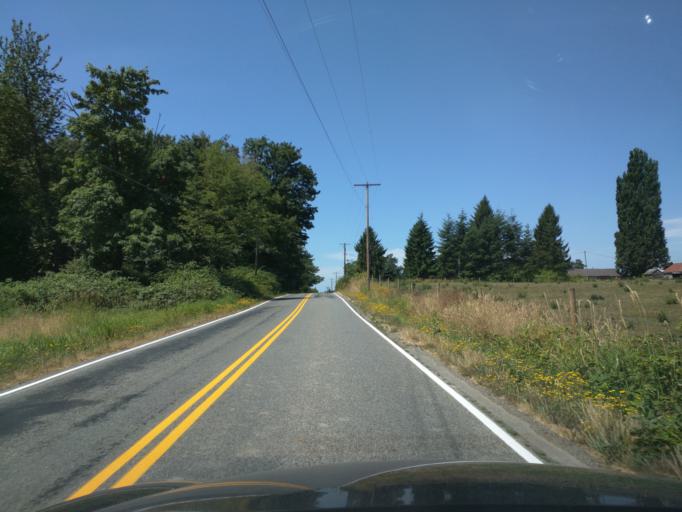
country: CA
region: British Columbia
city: Langley
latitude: 48.9648
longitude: -122.5711
